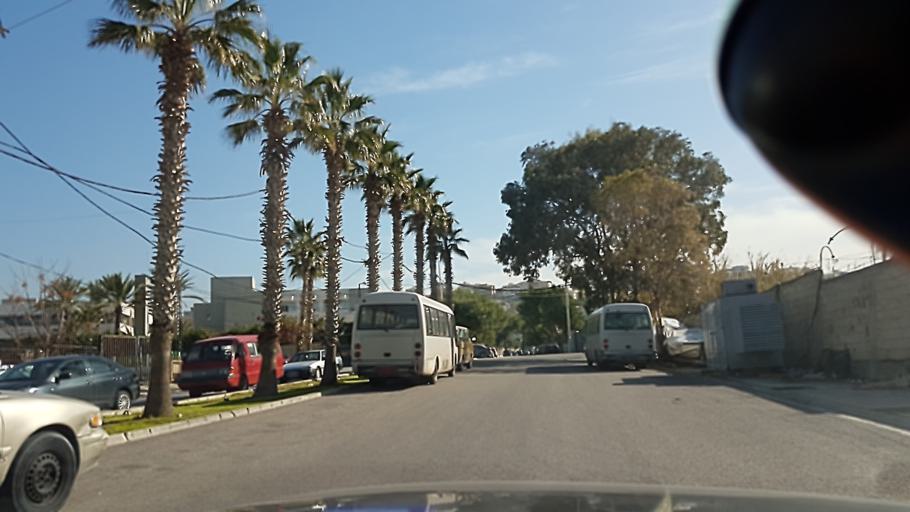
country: LB
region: Liban-Sud
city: Sidon
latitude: 33.5817
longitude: 35.3871
